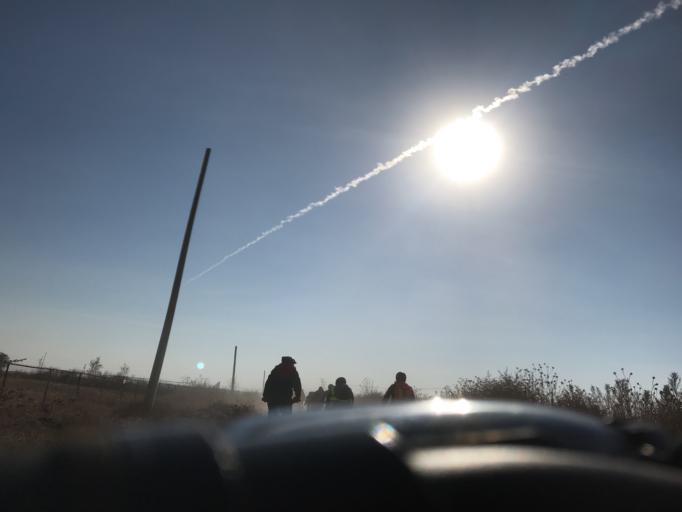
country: MX
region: Mexico
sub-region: Nextlalpan
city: Ex-Hacienda Santa Ines
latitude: 19.6974
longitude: -99.0750
